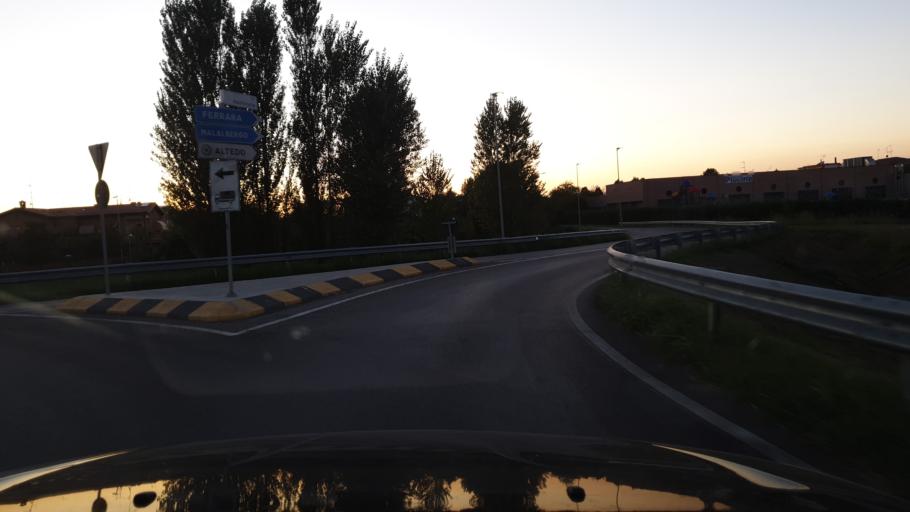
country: IT
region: Emilia-Romagna
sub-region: Provincia di Bologna
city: Altedo
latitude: 44.6608
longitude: 11.4917
